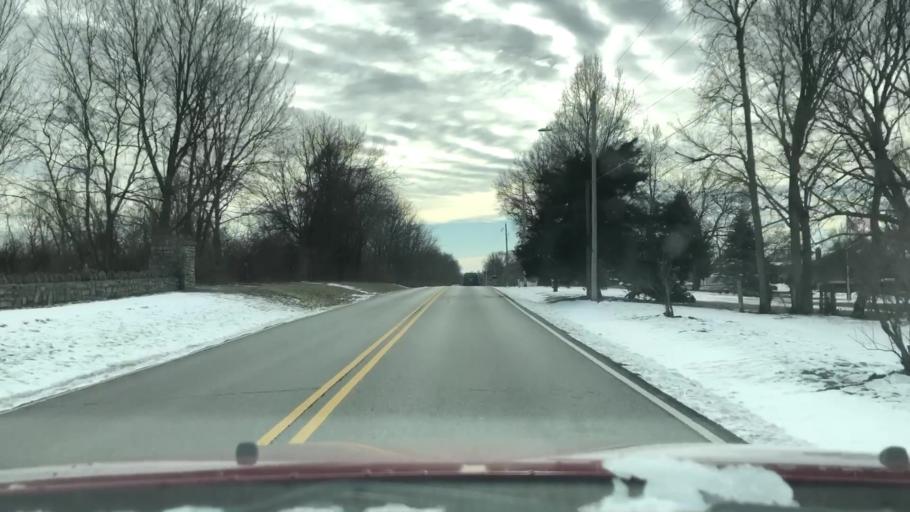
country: US
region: Missouri
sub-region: Jackson County
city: Greenwood
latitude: 38.8648
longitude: -94.3419
